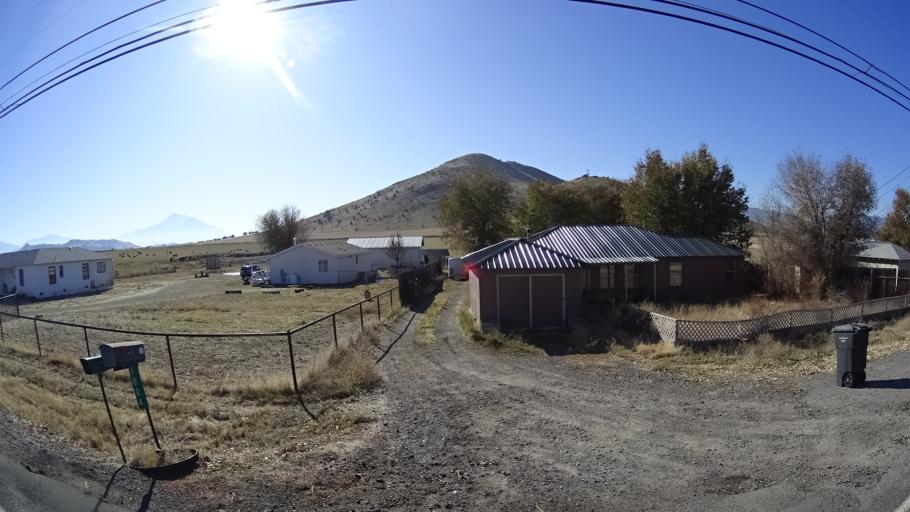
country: US
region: California
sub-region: Siskiyou County
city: Montague
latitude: 41.7248
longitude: -122.5136
